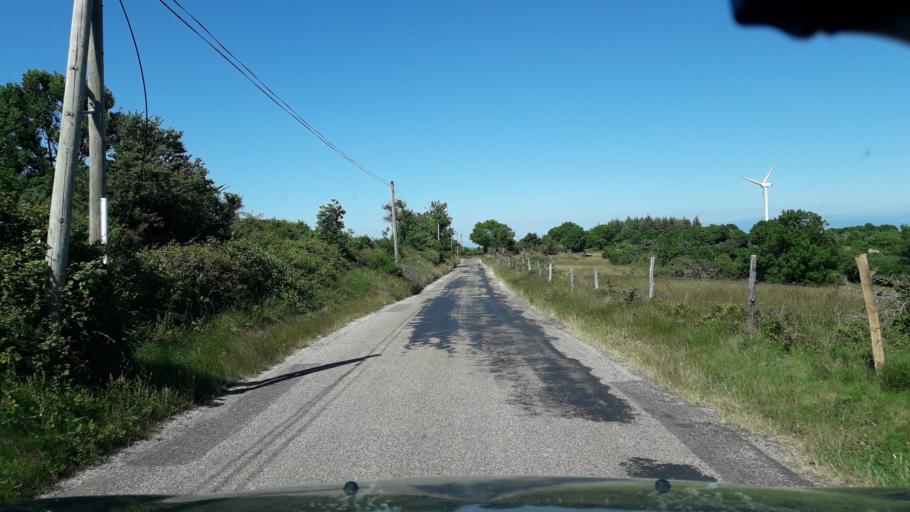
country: FR
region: Rhone-Alpes
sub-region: Departement de l'Ardeche
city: Saint-Priest
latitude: 44.6849
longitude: 4.5613
